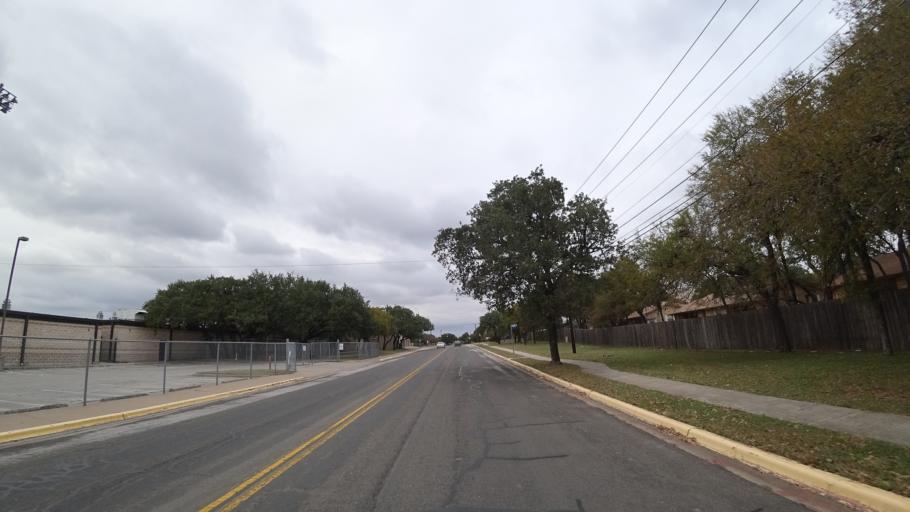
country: US
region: Texas
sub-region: Williamson County
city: Round Rock
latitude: 30.5075
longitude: -97.6945
